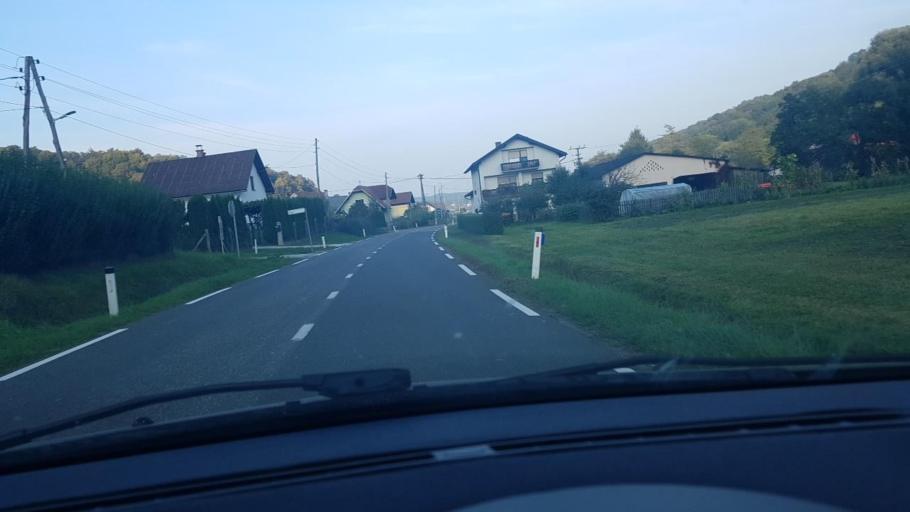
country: SI
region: Majsperk
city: Majsperk
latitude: 46.3290
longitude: 15.7238
